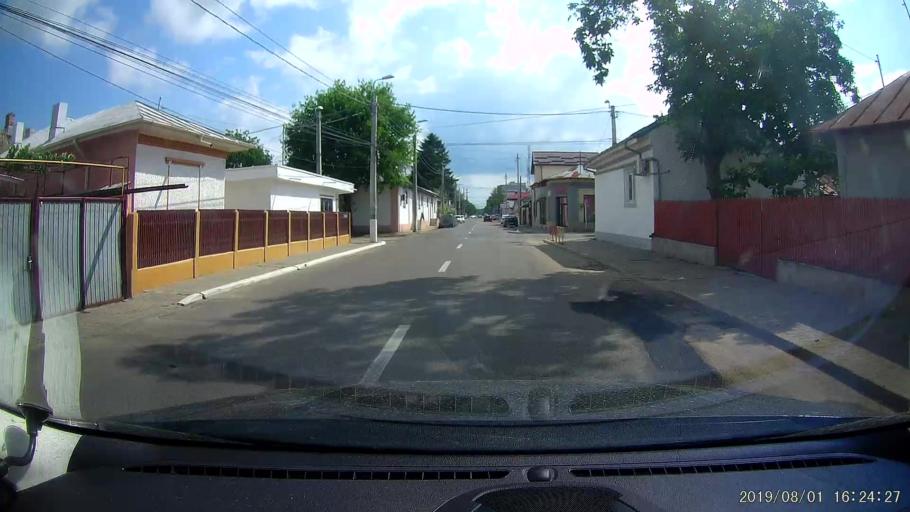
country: RO
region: Calarasi
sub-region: Municipiul Calarasi
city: Calarasi
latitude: 44.1958
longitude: 27.3296
